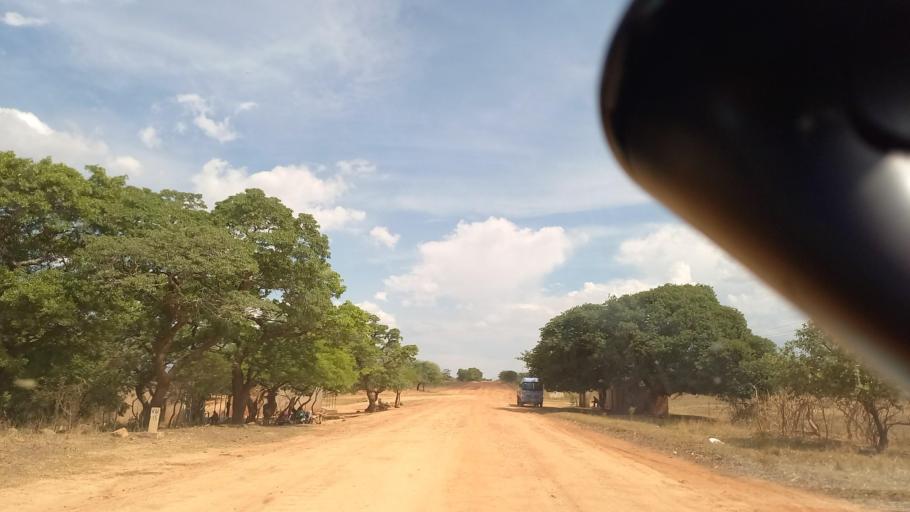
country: ZM
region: Lusaka
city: Kafue
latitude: -16.1341
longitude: 28.0495
